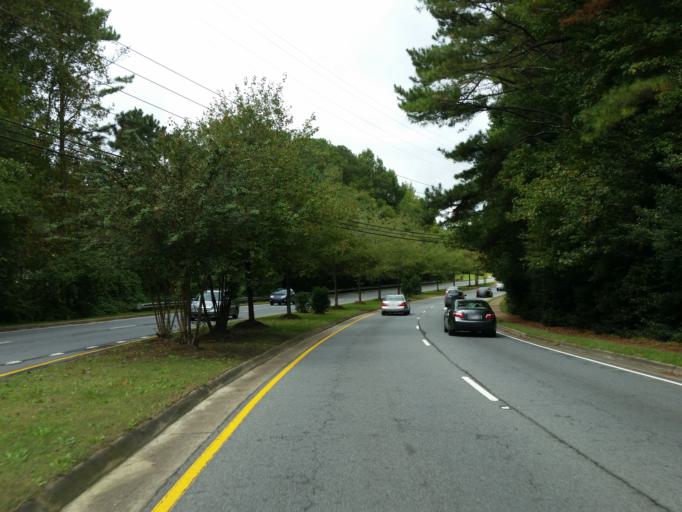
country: US
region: Georgia
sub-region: Fulton County
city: Roswell
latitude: 33.9958
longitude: -84.4342
